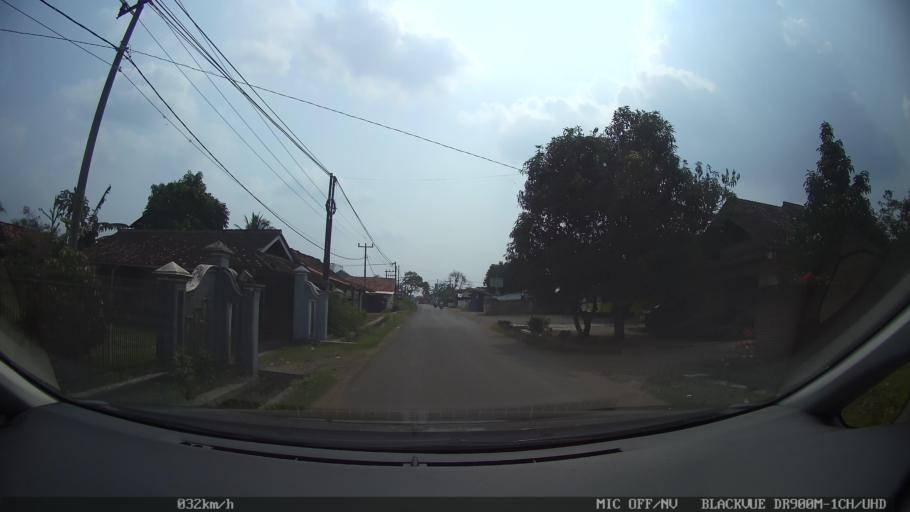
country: ID
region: Lampung
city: Gadingrejo
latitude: -5.3505
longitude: 105.0236
